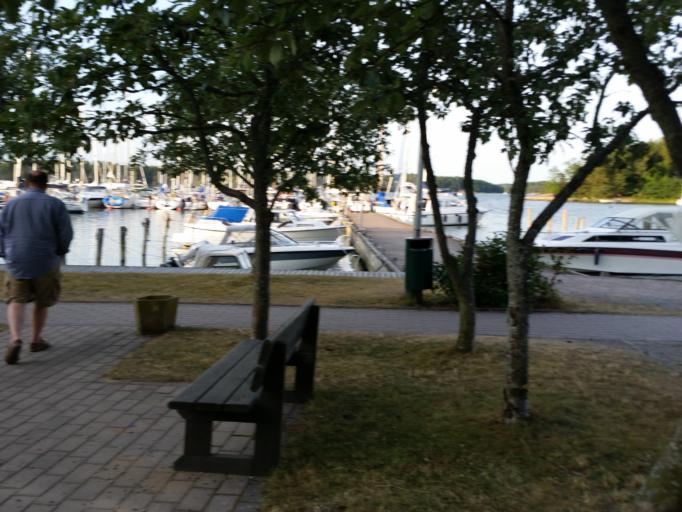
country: FI
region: Varsinais-Suomi
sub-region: Aboland-Turunmaa
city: Nagu
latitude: 60.1945
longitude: 21.9106
